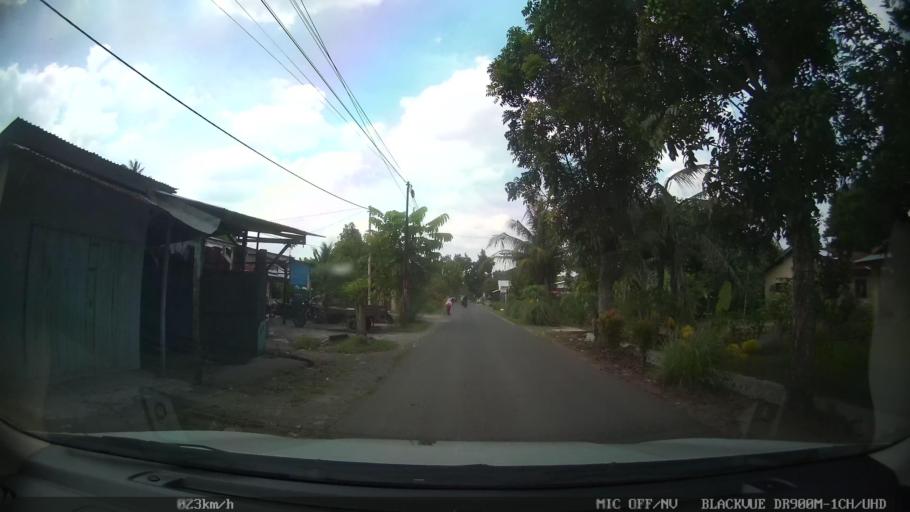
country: ID
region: North Sumatra
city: Binjai
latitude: 3.6292
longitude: 98.5172
